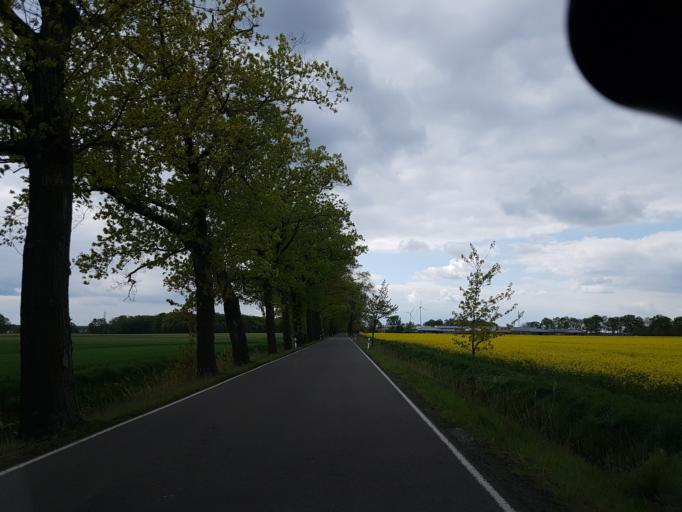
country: DE
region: Brandenburg
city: Bronkow
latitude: 51.6163
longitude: 13.9143
